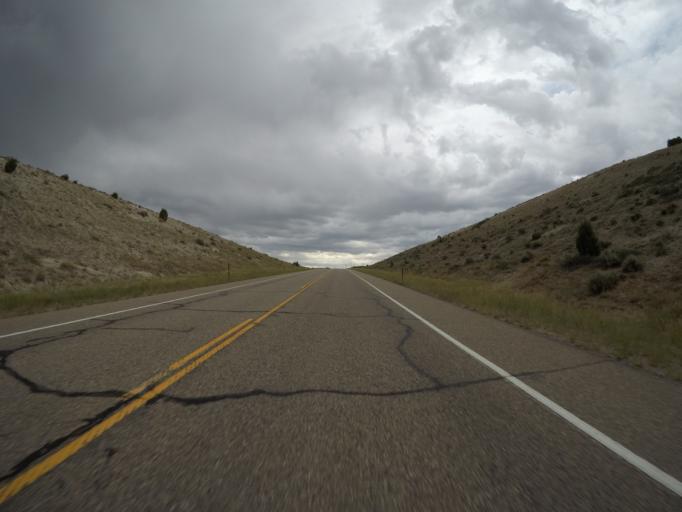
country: US
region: Colorado
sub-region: Rio Blanco County
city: Rangely
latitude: 40.3683
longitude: -108.4002
